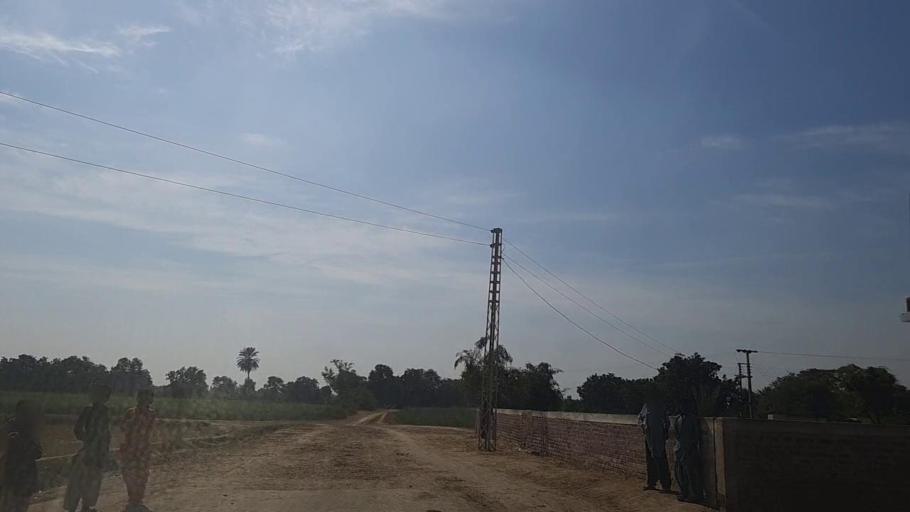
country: PK
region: Sindh
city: Mirpur Khas
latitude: 25.4667
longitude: 68.9624
